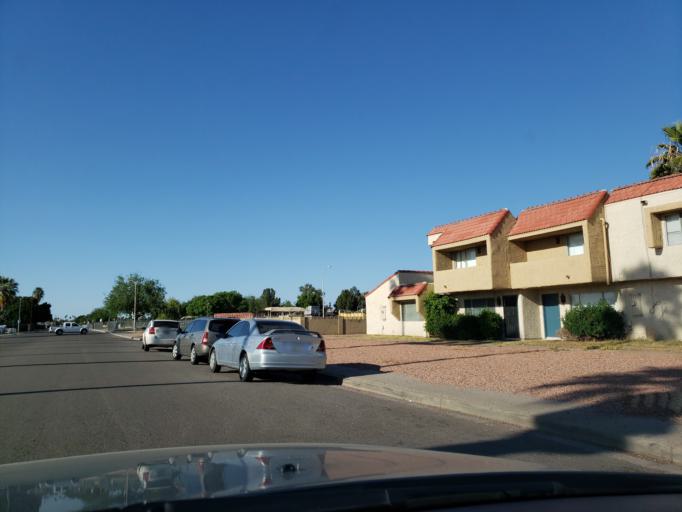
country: US
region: Arizona
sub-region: Maricopa County
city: Glendale
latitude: 33.5286
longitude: -112.1644
